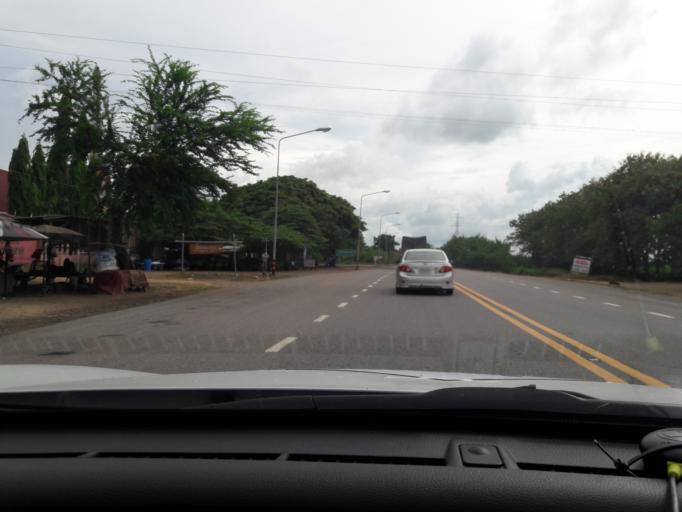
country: TH
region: Nakhon Sawan
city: Tak Fa
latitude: 15.4180
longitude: 100.5159
